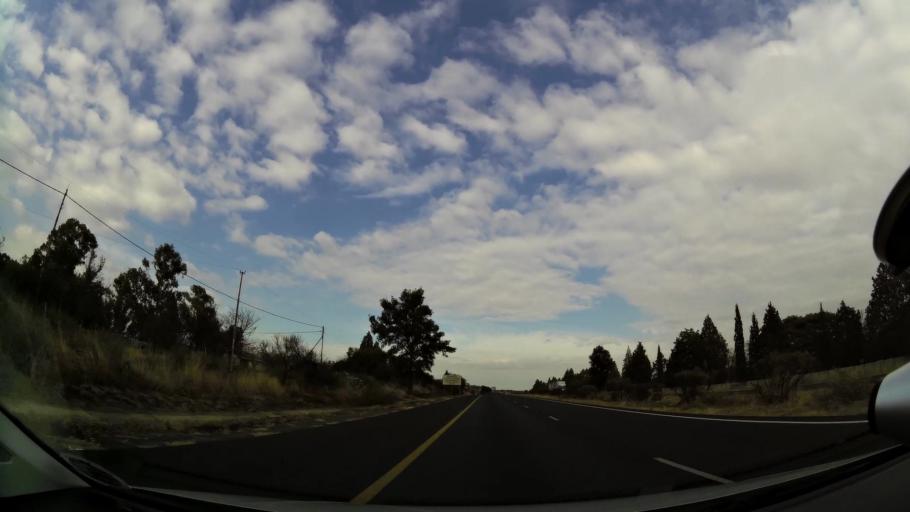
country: ZA
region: Orange Free State
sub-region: Fezile Dabi District Municipality
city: Kroonstad
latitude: -27.6785
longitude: 27.2489
